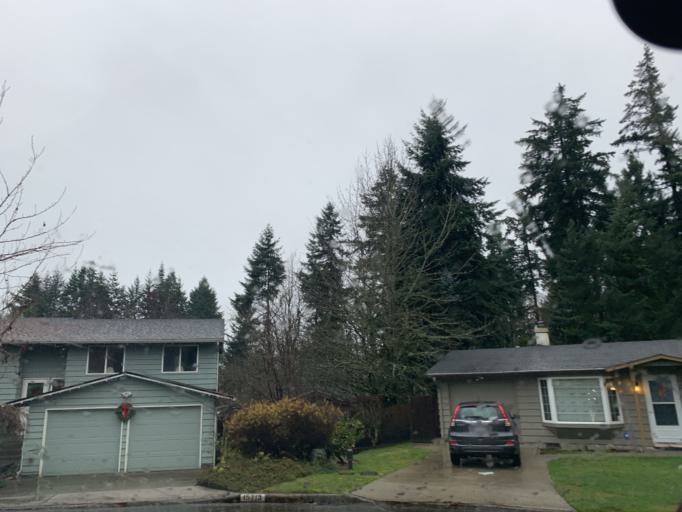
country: US
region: Washington
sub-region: King County
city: Woodinville
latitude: 47.7424
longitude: -122.1716
